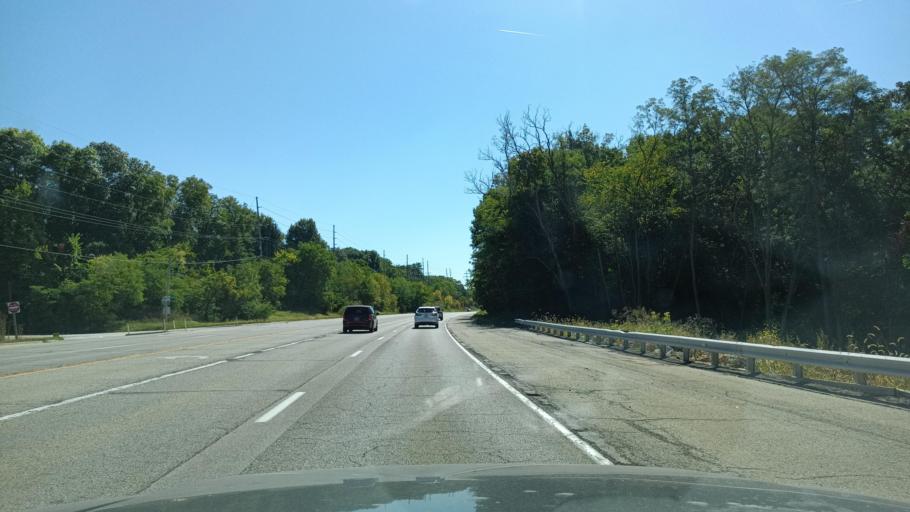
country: US
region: Illinois
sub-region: Peoria County
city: Peoria Heights
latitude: 40.7651
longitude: -89.6422
